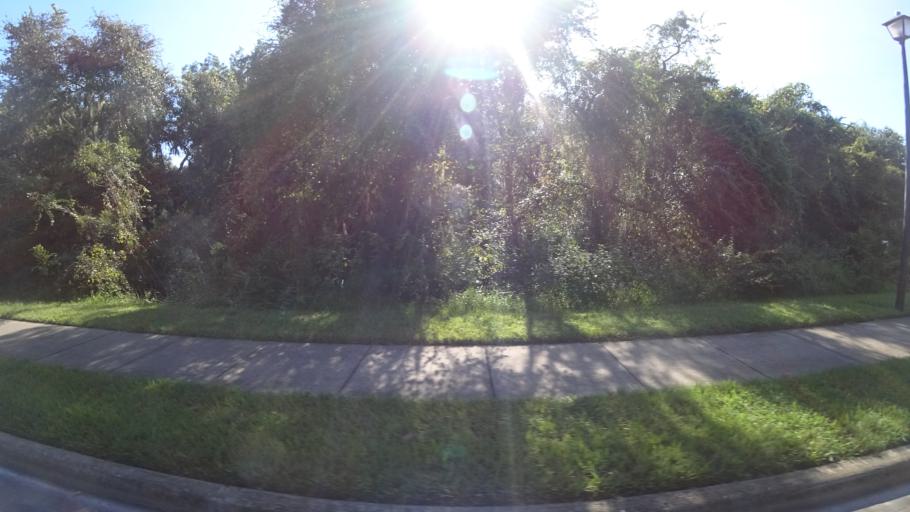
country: US
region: Florida
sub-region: Sarasota County
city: Desoto Lakes
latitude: 27.4177
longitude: -82.4648
